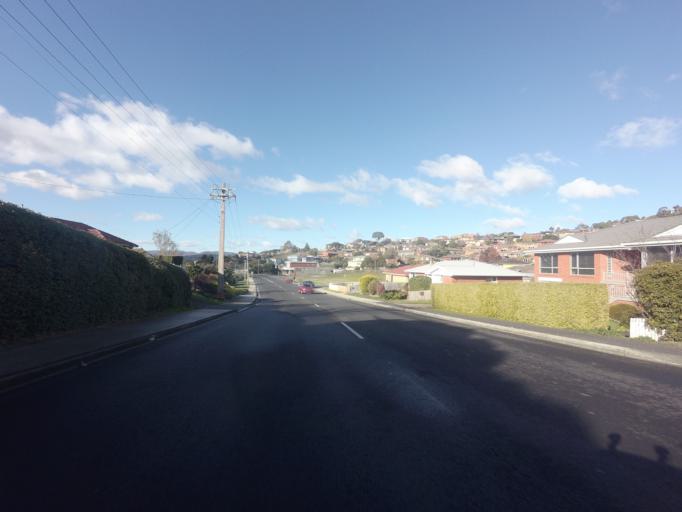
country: AU
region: Tasmania
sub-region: Glenorchy
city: Berriedale
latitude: -42.8158
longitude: 147.2491
